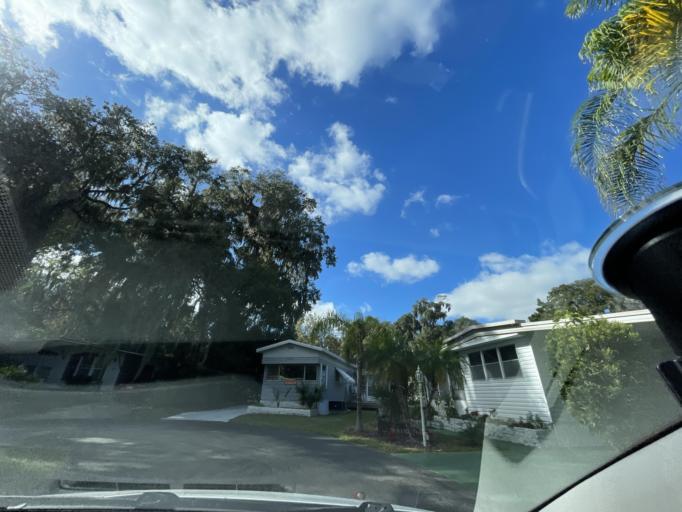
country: US
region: Florida
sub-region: Volusia County
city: South Daytona
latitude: 29.1687
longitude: -81.0275
